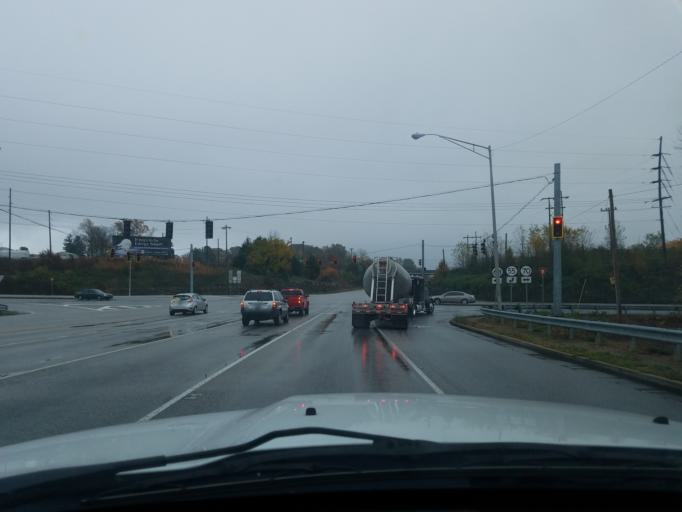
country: US
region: Kentucky
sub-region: Taylor County
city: Campbellsville
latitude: 37.3387
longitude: -85.3608
